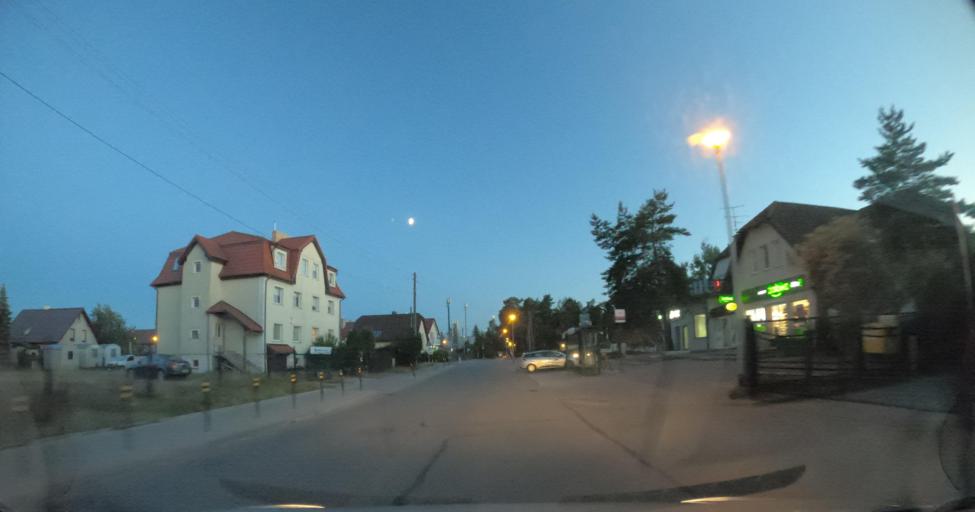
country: PL
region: Pomeranian Voivodeship
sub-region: Gdynia
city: Wielki Kack
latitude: 54.4302
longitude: 18.4700
